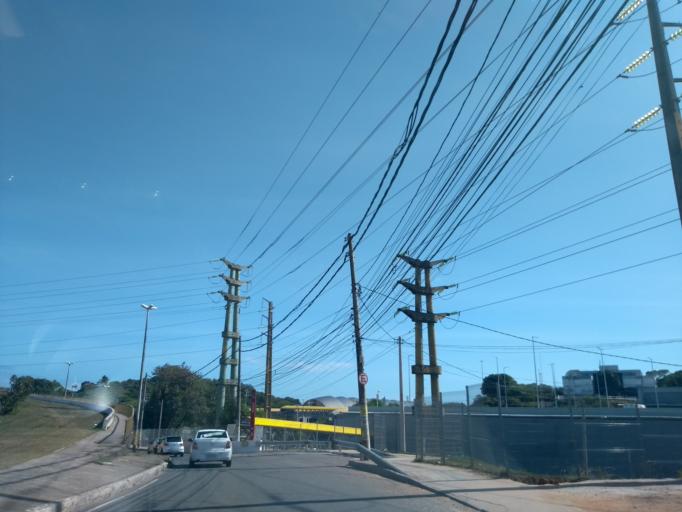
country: BR
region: Bahia
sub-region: Salvador
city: Salvador
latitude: -12.9420
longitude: -38.4208
